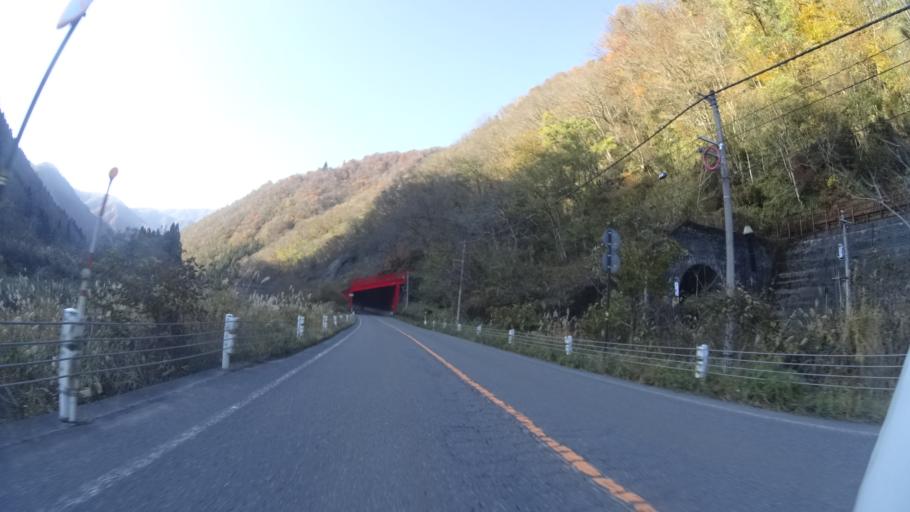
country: JP
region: Fukui
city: Ono
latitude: 35.9046
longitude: 136.6477
